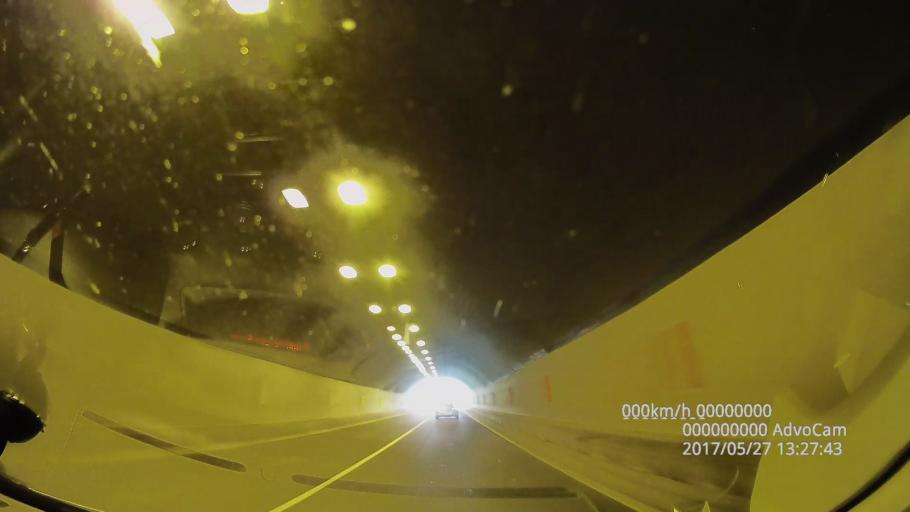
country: BG
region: Blagoevgrad
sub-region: Obshtina Simitli
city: Simitli
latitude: 41.9367
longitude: 23.1026
